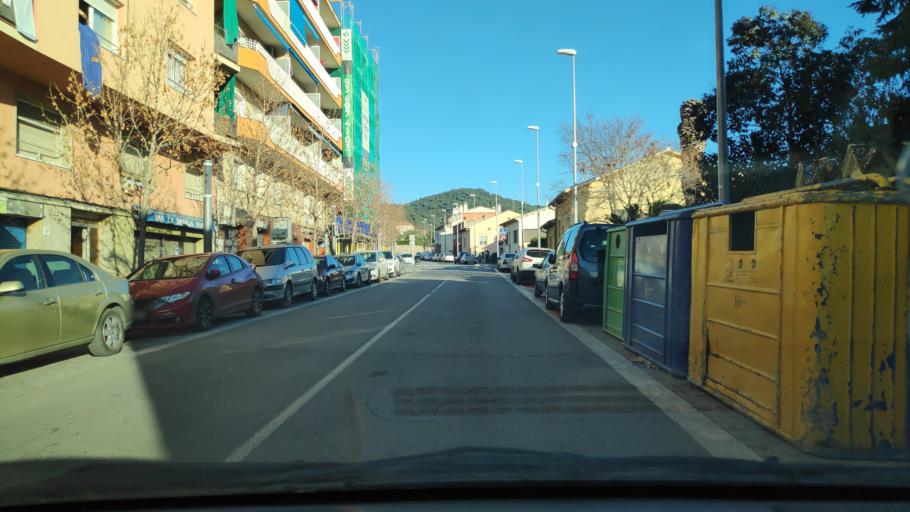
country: ES
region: Catalonia
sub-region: Provincia de Barcelona
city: Montmelo
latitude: 41.5274
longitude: 2.2354
